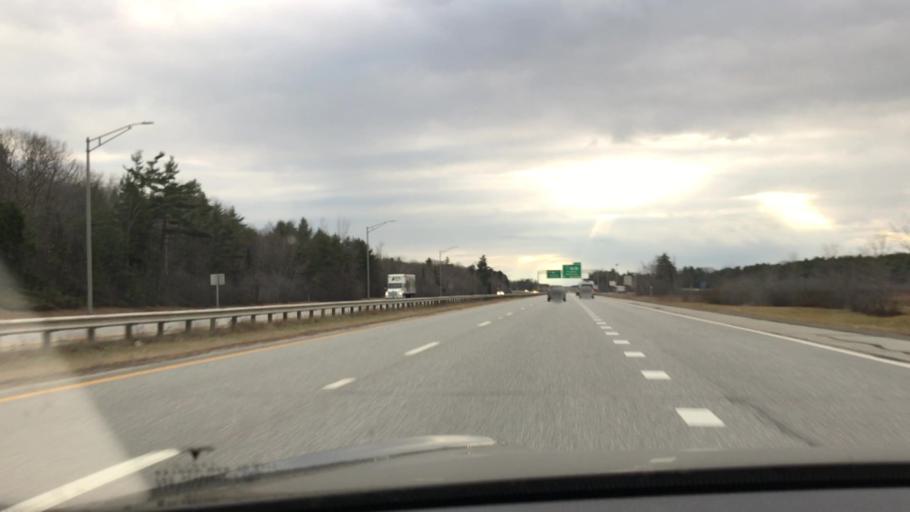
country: US
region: Maine
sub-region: Kennebec County
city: Gardiner
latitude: 44.2272
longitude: -69.8153
